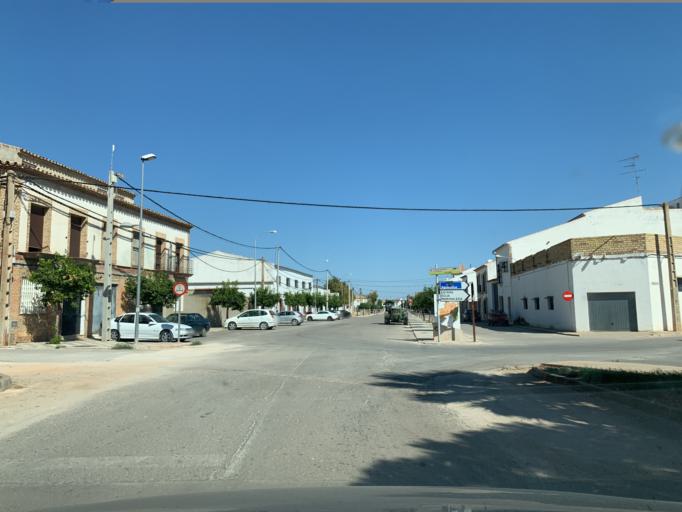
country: ES
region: Andalusia
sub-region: Provincia de Sevilla
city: El Rubio
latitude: 37.3532
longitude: -4.9962
